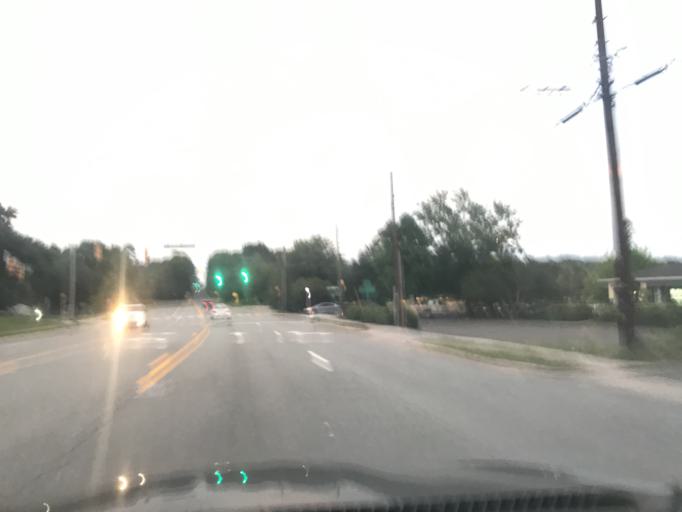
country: US
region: North Carolina
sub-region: Orange County
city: Chapel Hill
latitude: 35.9362
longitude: -79.0272
